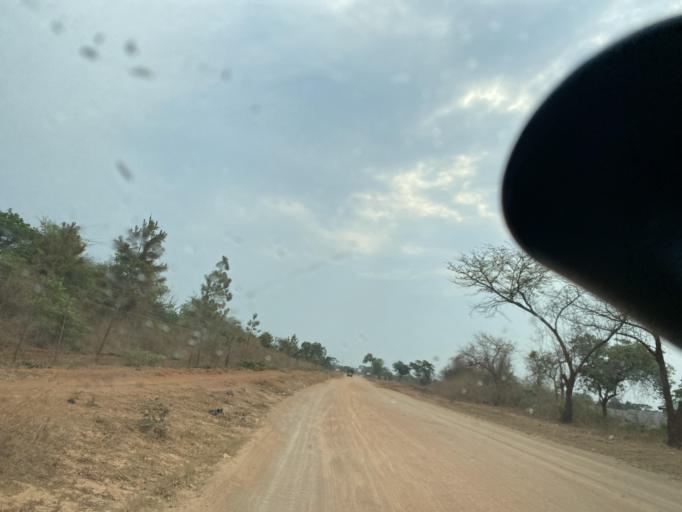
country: ZM
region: Lusaka
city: Lusaka
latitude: -15.2874
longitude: 28.2909
